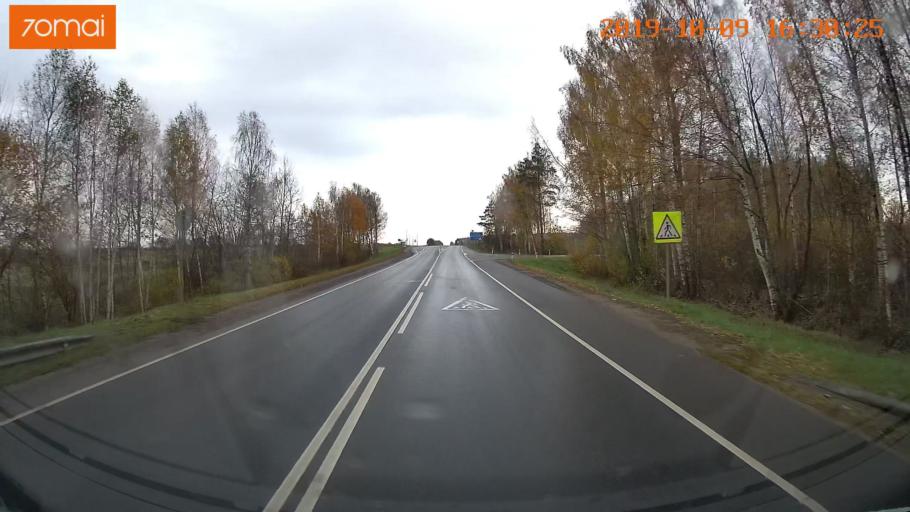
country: RU
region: Kostroma
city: Oktyabr'skiy
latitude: 57.6195
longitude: 40.9400
